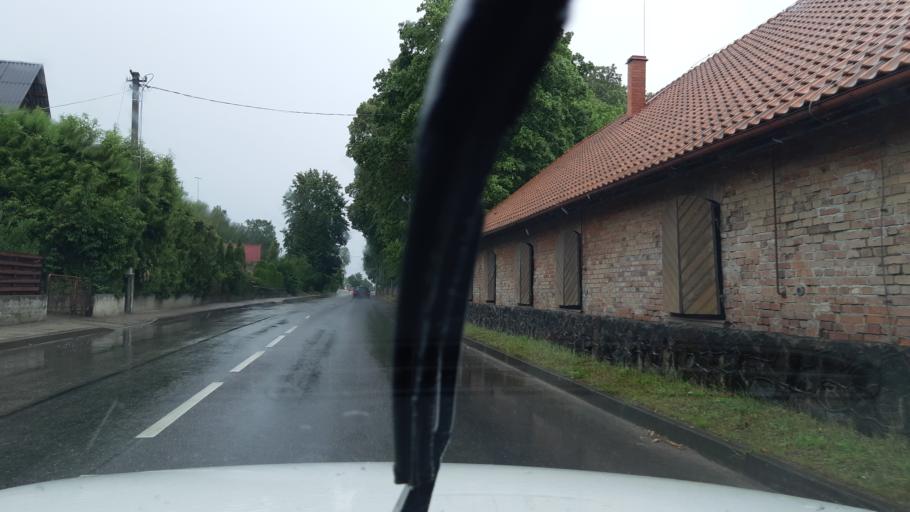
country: LT
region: Taurages apskritis
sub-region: Jurbarkas
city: Jurbarkas
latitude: 55.0827
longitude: 22.7485
